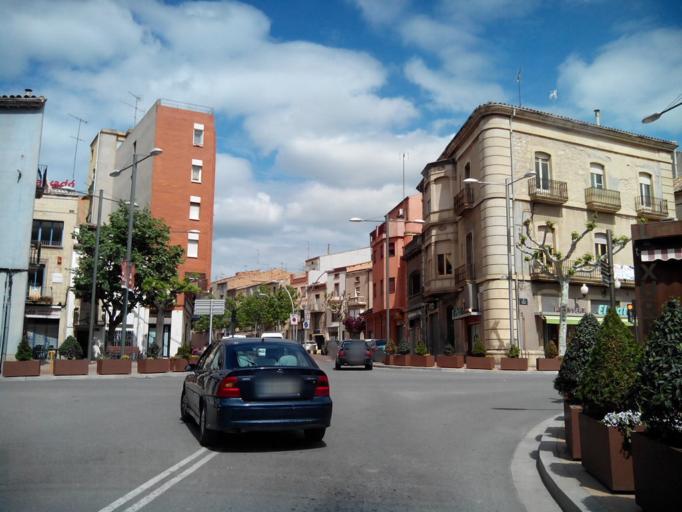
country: ES
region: Catalonia
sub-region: Provincia de Lleida
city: Tarrega
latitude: 41.6486
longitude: 1.1404
